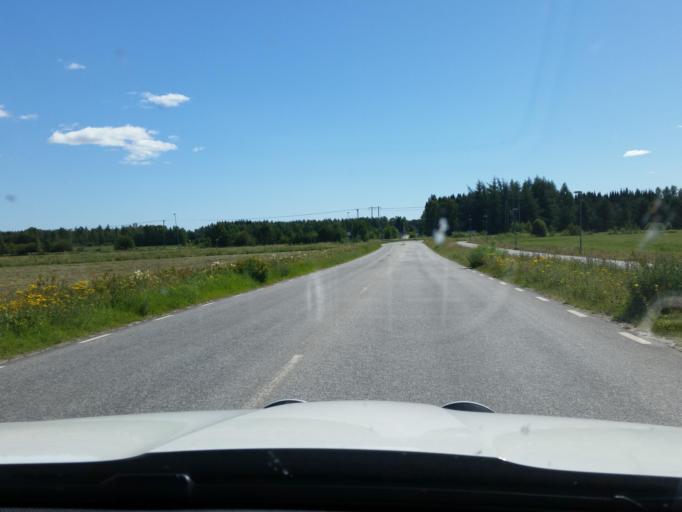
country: SE
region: Norrbotten
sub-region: Pitea Kommun
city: Bergsviken
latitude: 65.2988
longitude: 21.4104
